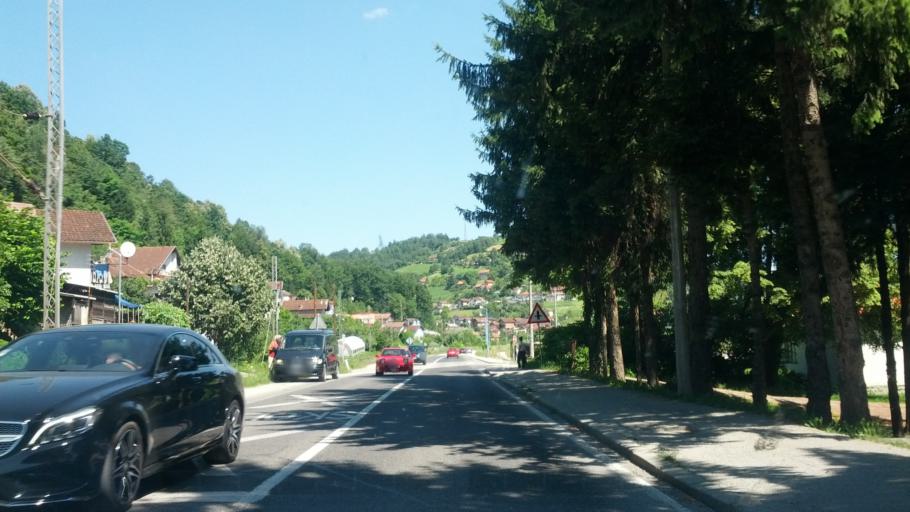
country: BA
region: Federation of Bosnia and Herzegovina
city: Bosanska Krupa
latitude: 44.8900
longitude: 16.1543
